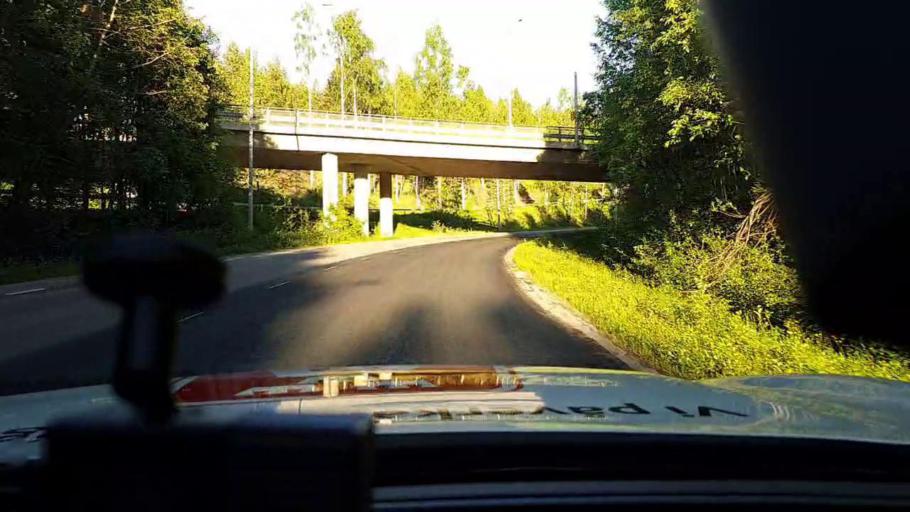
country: SE
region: Norrbotten
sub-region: Lulea Kommun
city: Lulea
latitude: 65.6088
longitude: 22.1862
